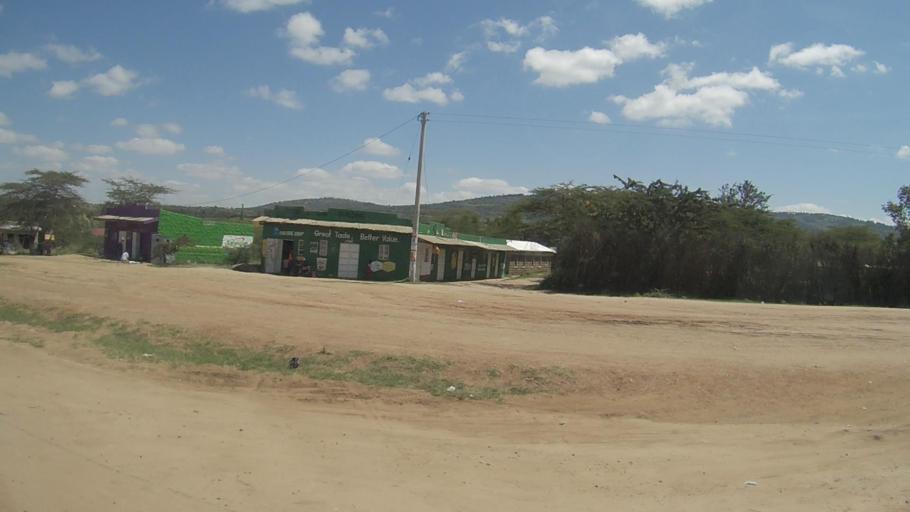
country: KE
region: Machakos
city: Machakos
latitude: -1.5327
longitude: 37.1976
